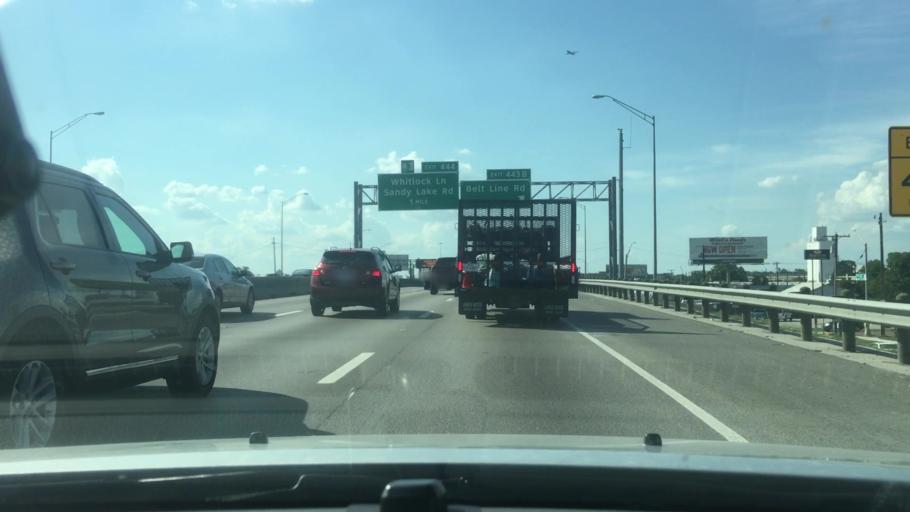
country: US
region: Texas
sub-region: Dallas County
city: Carrollton
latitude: 32.9463
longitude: -96.9054
